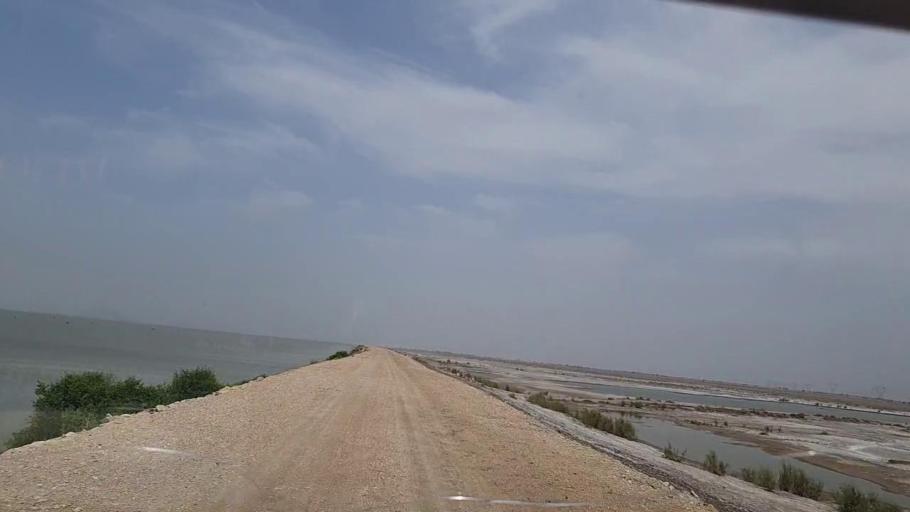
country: PK
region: Sindh
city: Sehwan
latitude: 26.4114
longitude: 67.7922
